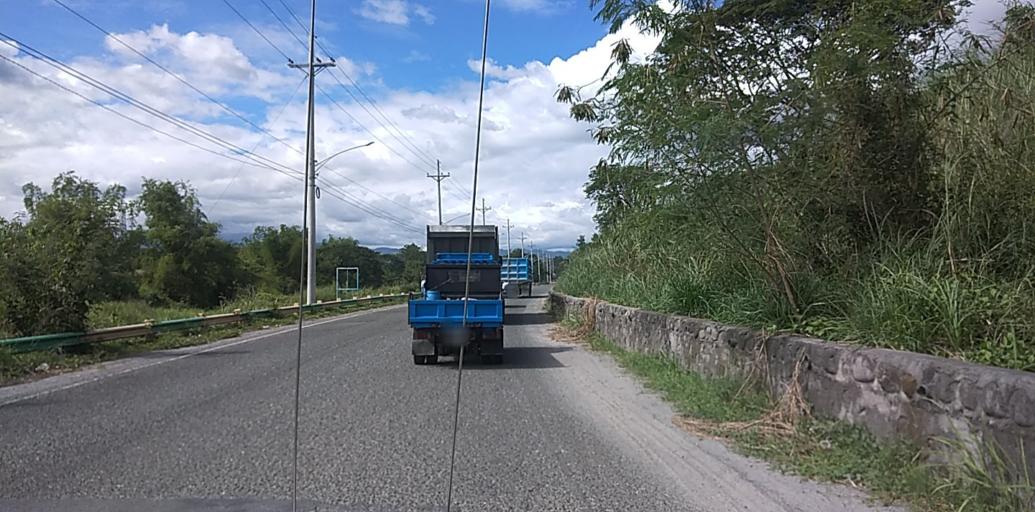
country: PH
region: Central Luzon
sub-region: Province of Pampanga
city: Dolores
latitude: 15.0891
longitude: 120.5379
